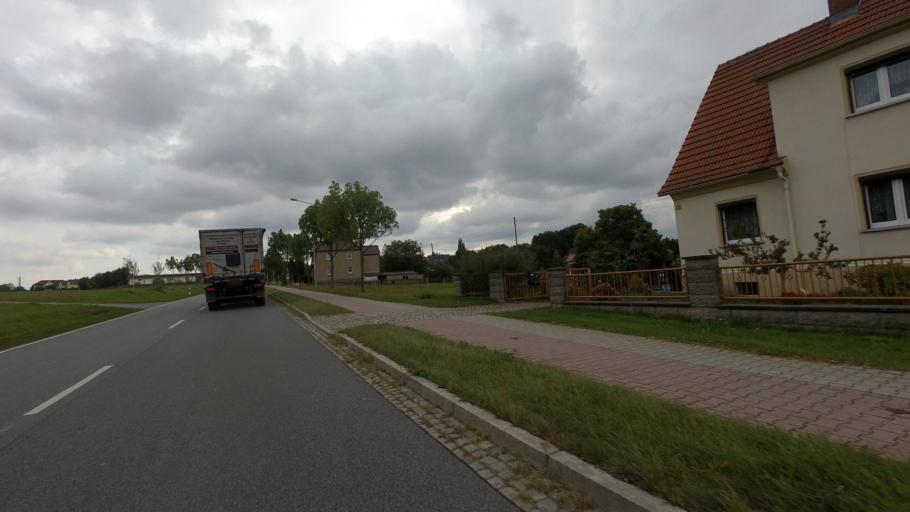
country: DE
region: Saxony
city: Radibor
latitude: 51.2168
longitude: 14.3910
